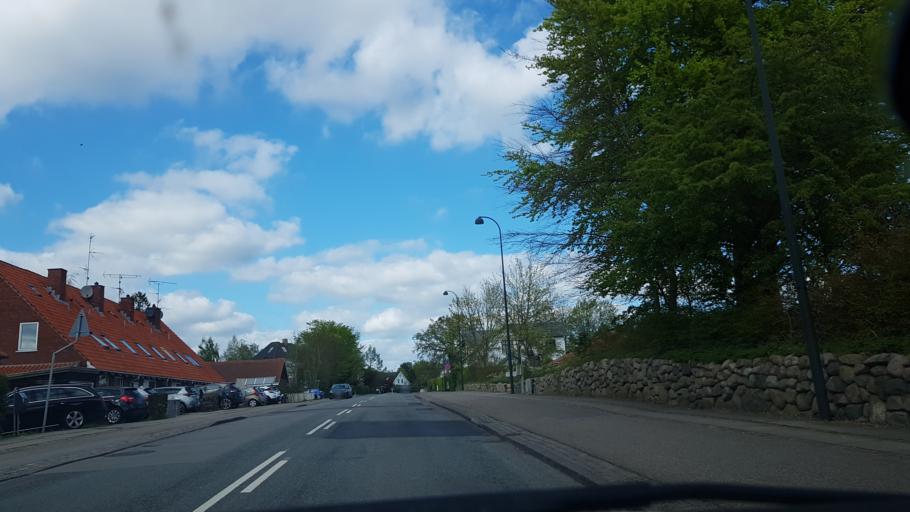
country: DK
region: Capital Region
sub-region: Rudersdal Kommune
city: Holte
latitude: 55.8140
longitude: 12.4802
